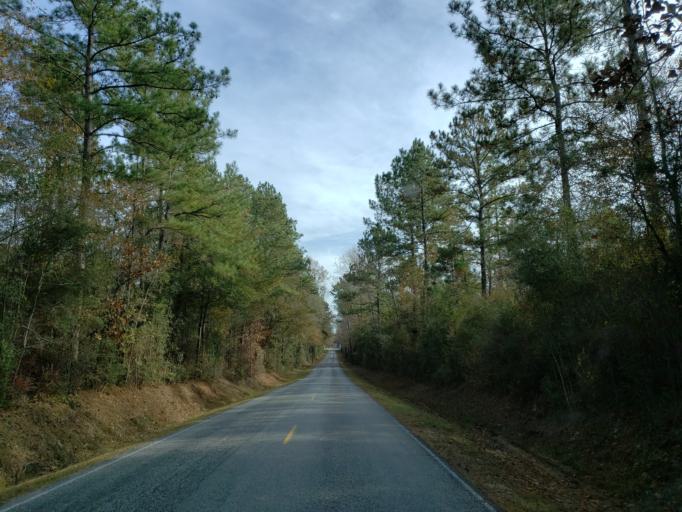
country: US
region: Mississippi
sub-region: Forrest County
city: Rawls Springs
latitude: 31.4039
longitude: -89.3975
